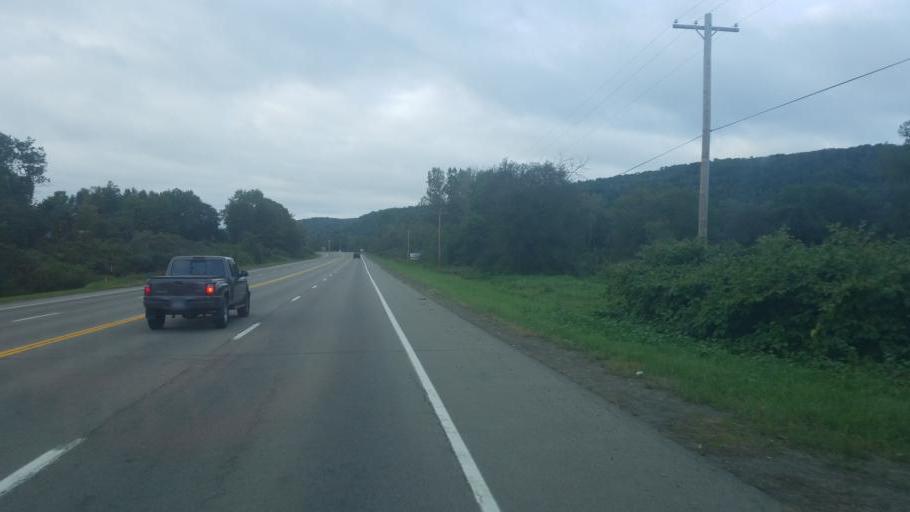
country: US
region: New York
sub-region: Cattaraugus County
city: Weston Mills
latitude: 42.1669
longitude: -78.3919
